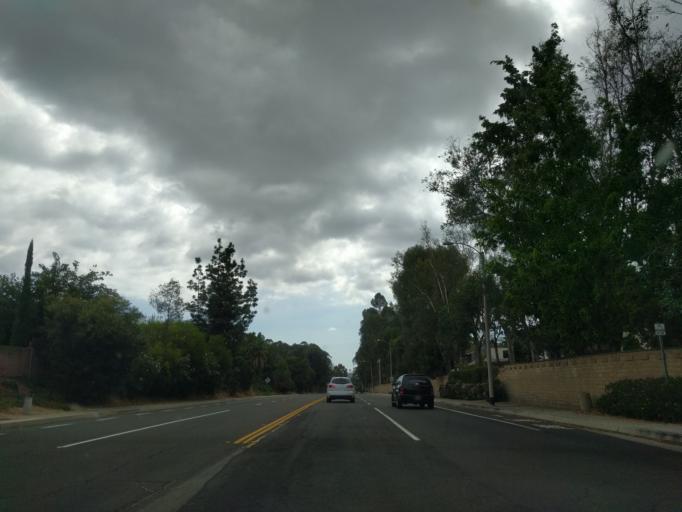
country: US
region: California
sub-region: Orange County
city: Lake Forest
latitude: 33.6365
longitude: -117.6923
